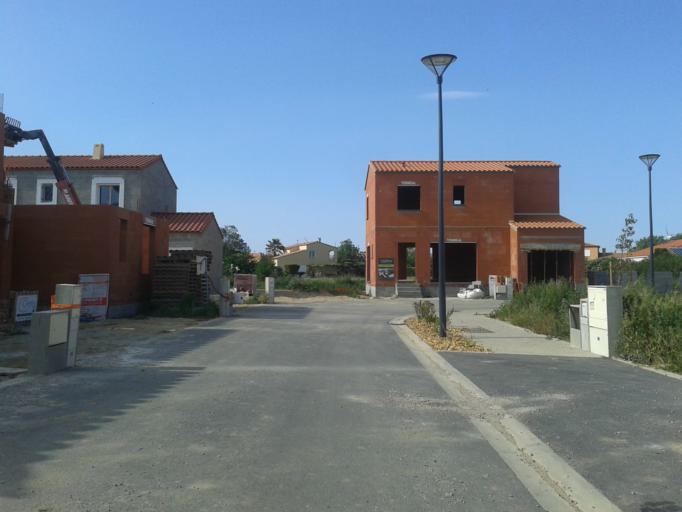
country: FR
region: Languedoc-Roussillon
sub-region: Departement des Pyrenees-Orientales
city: Pezilla-la-Riviere
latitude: 42.6968
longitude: 2.7772
